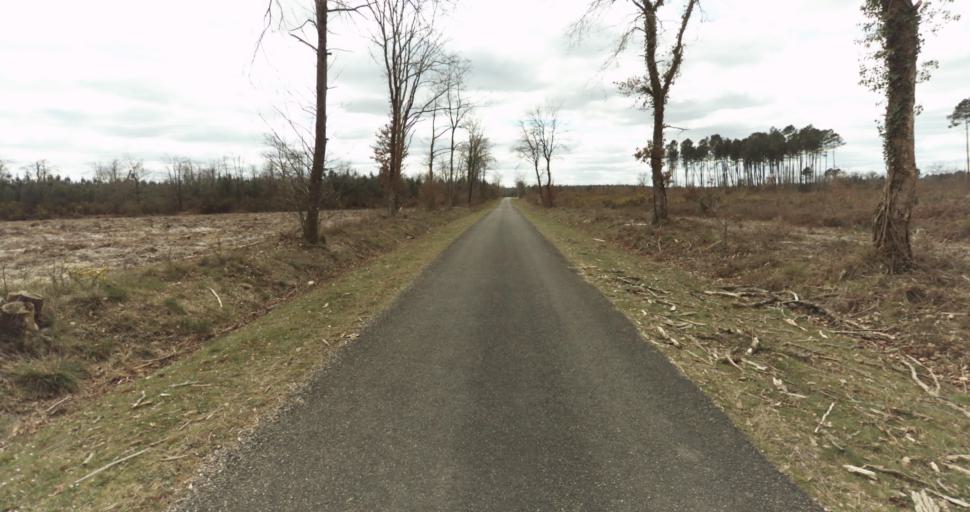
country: FR
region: Aquitaine
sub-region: Departement des Landes
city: Roquefort
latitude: 44.0649
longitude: -0.3984
